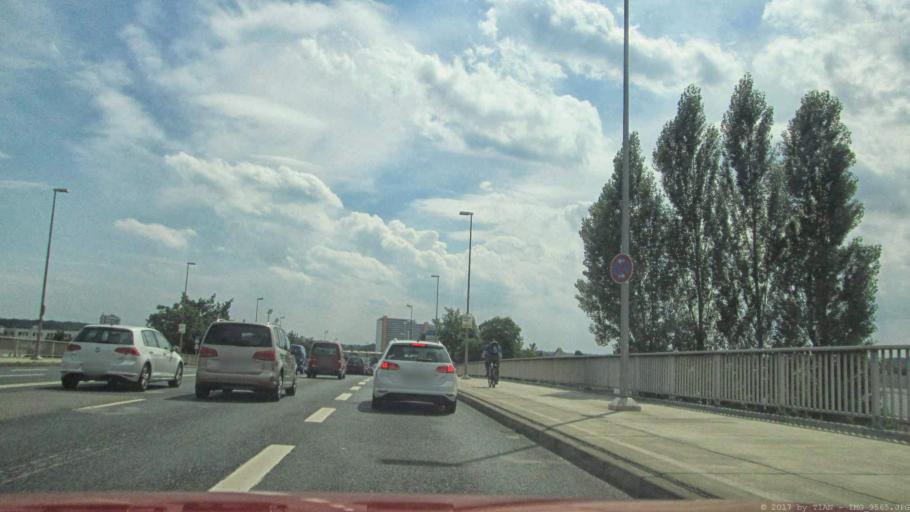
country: DE
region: Lower Saxony
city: Wolfsburg
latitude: 52.4304
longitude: 10.7992
